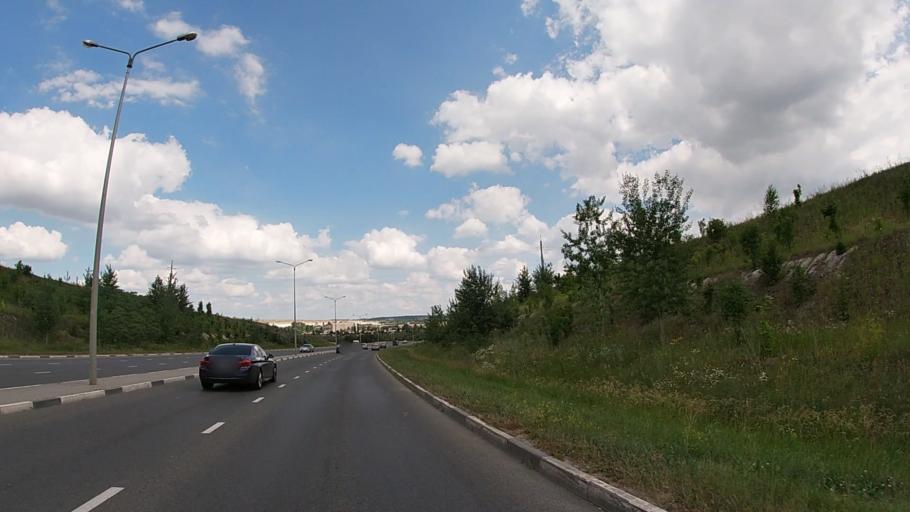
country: RU
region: Belgorod
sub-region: Belgorodskiy Rayon
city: Belgorod
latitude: 50.6038
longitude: 36.5299
